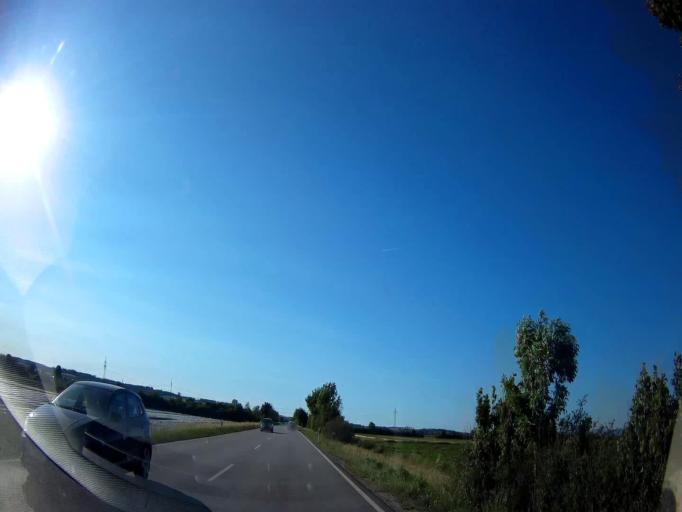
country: DE
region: Bavaria
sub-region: Lower Bavaria
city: Pilsting
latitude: 48.7171
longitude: 12.6704
